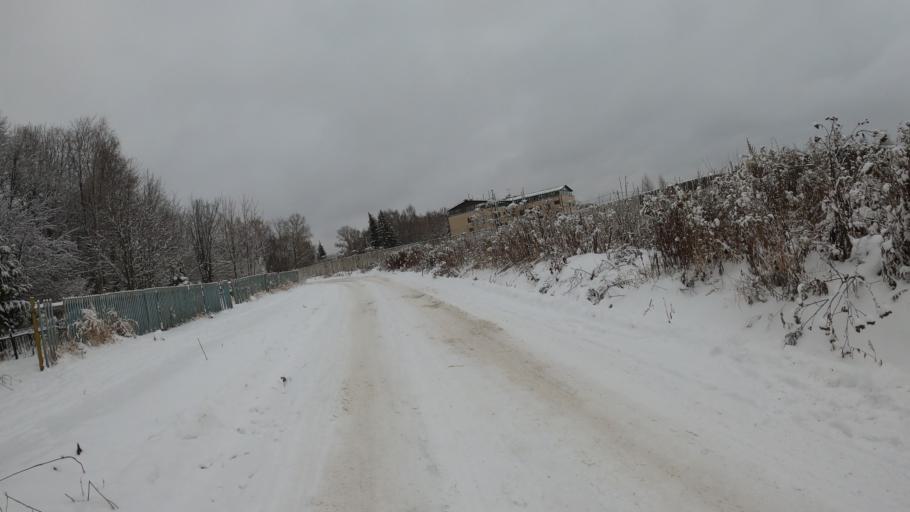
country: RU
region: Jaroslavl
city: Pereslavl'-Zalesskiy
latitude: 56.7537
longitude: 38.8619
